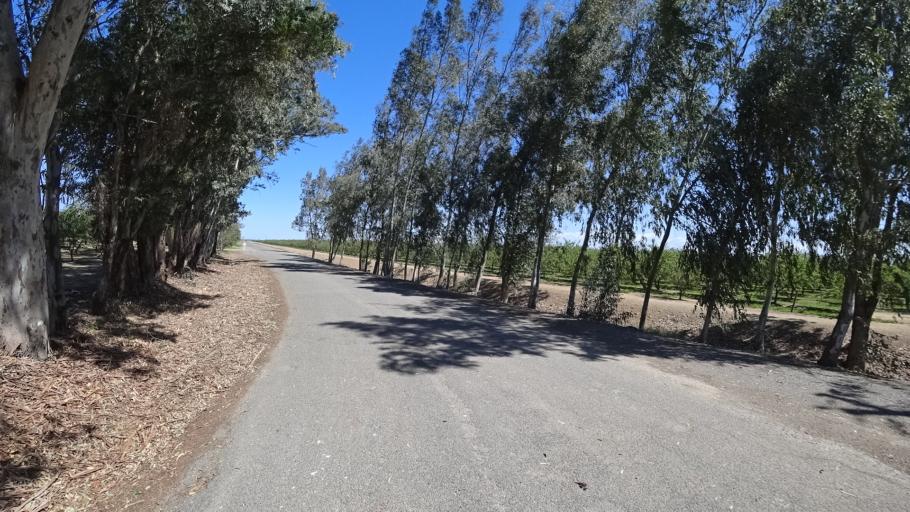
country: US
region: California
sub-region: Glenn County
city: Orland
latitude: 39.6818
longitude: -122.1221
